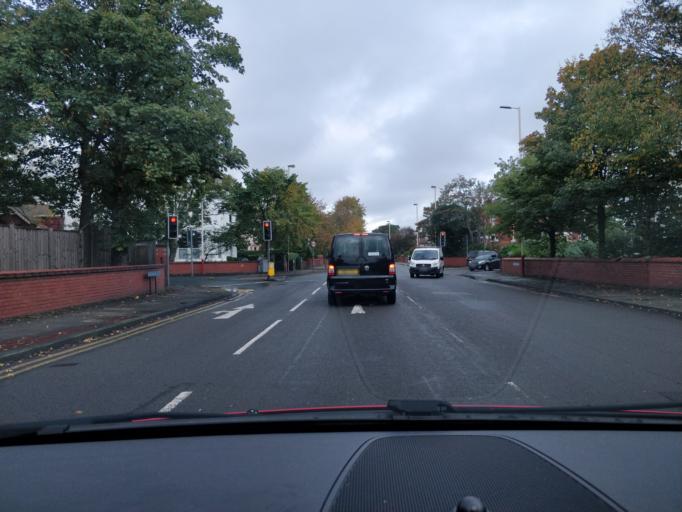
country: GB
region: England
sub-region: Sefton
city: Southport
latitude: 53.6294
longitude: -3.0117
